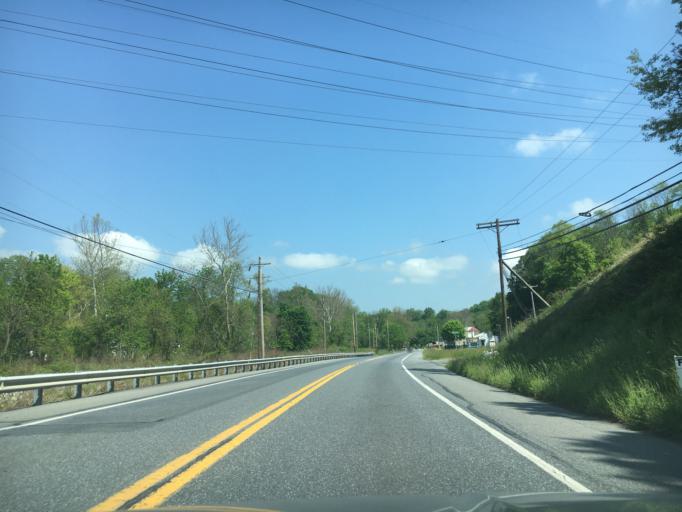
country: US
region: Pennsylvania
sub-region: Berks County
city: Boyertown
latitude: 40.3487
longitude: -75.6618
